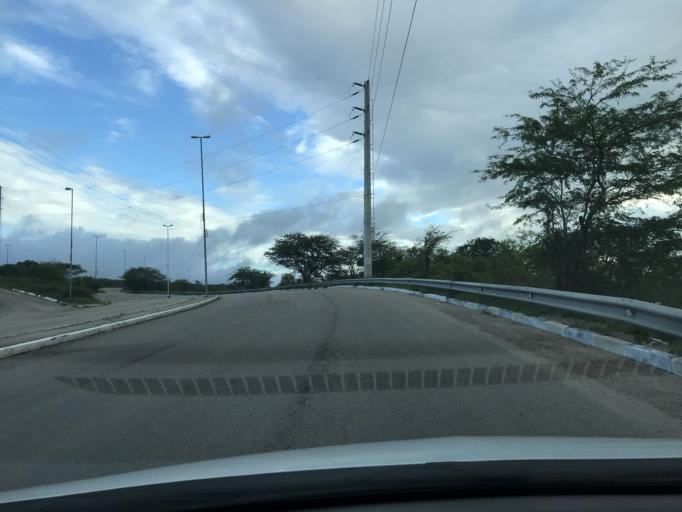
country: BR
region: Pernambuco
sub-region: Caruaru
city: Caruaru
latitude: -8.3052
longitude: -35.9420
